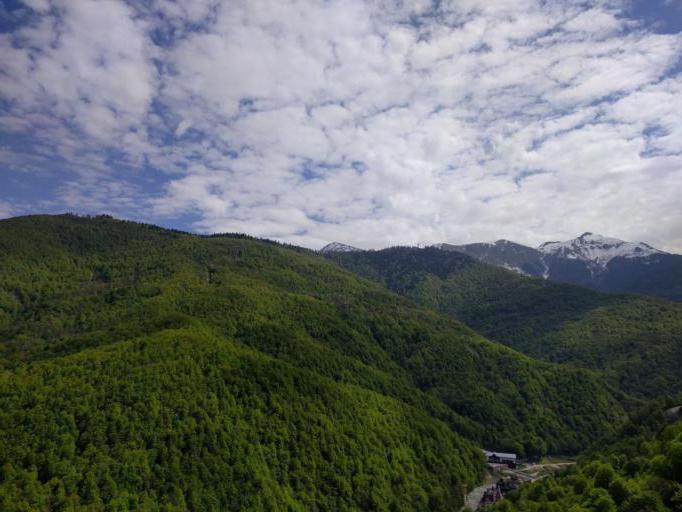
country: RU
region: Krasnodarskiy
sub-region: Sochi City
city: Krasnaya Polyana
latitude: 43.6683
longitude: 40.3036
